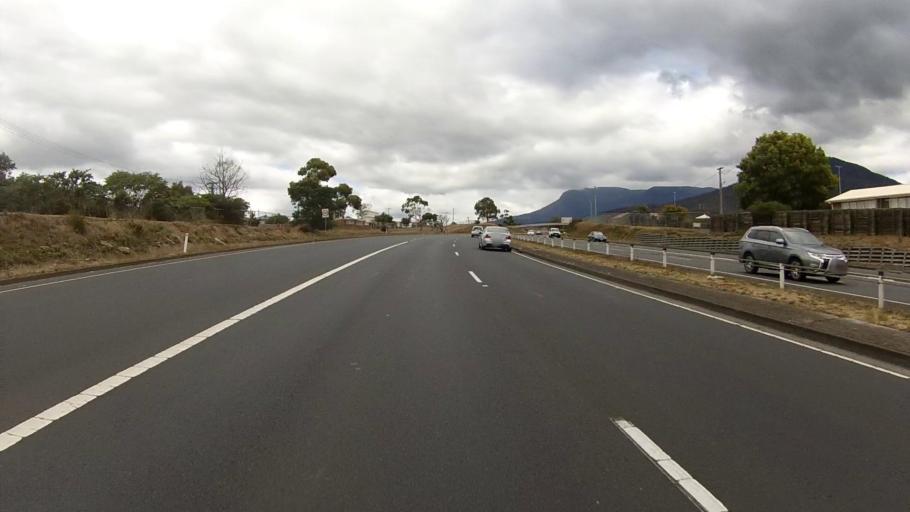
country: AU
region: Tasmania
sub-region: Glenorchy
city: Berriedale
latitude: -42.8016
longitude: 147.2497
